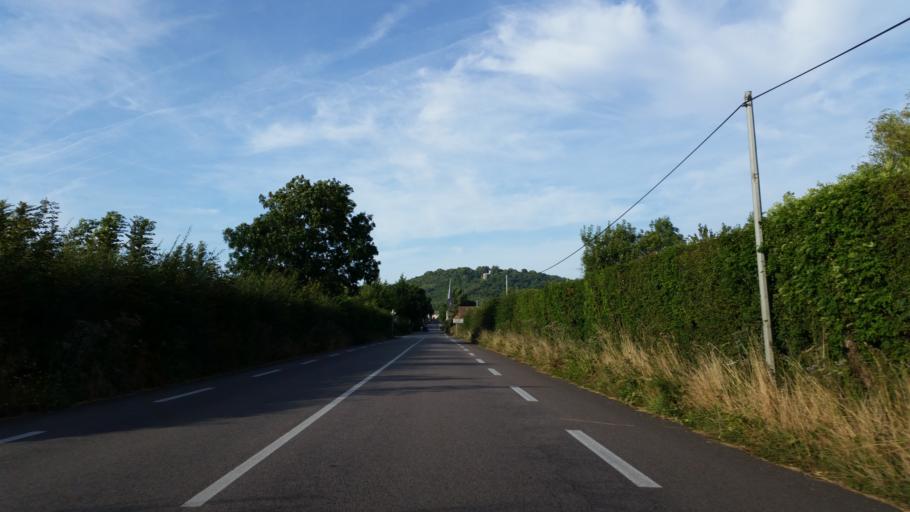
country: FR
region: Lower Normandy
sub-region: Departement du Calvados
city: Cambremer
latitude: 49.1118
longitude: 0.0089
